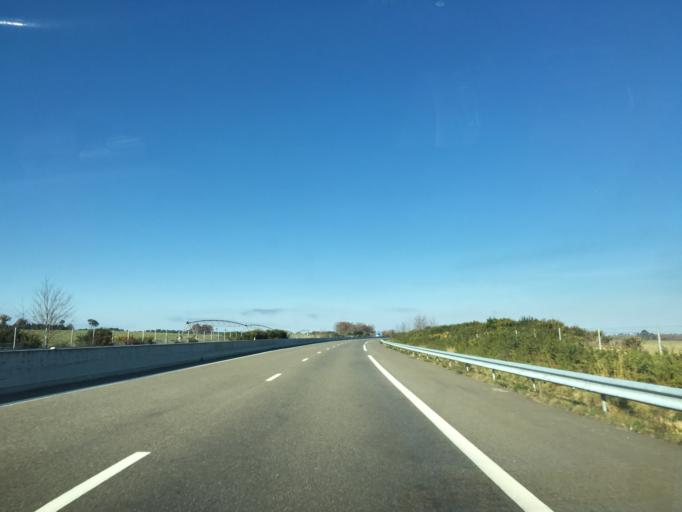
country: FR
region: Aquitaine
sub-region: Departement des Landes
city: Villeneuve-de-Marsan
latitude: 43.8587
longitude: -0.3514
